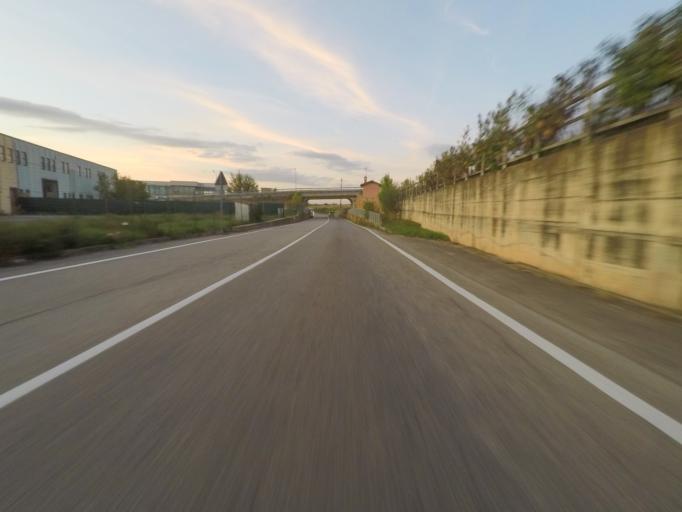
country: IT
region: Tuscany
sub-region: Provincia di Siena
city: Sinalunga
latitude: 43.2120
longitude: 11.7621
